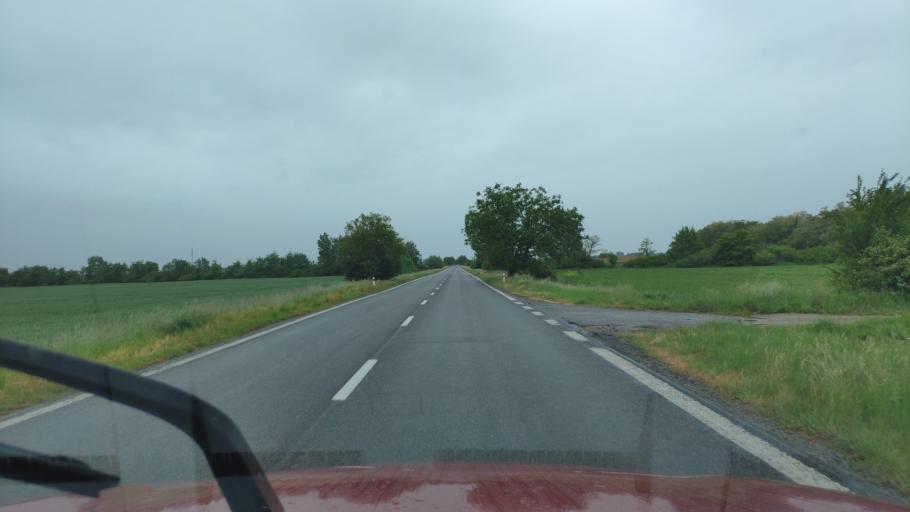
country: HU
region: Borsod-Abauj-Zemplen
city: Karcsa
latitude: 48.4174
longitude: 21.8314
